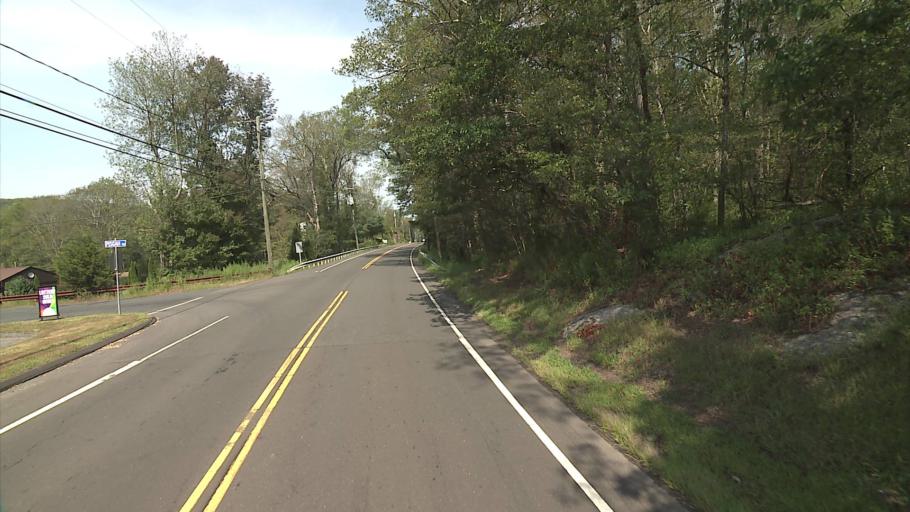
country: US
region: Connecticut
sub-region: Middlesex County
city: Durham
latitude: 41.4446
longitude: -72.6622
